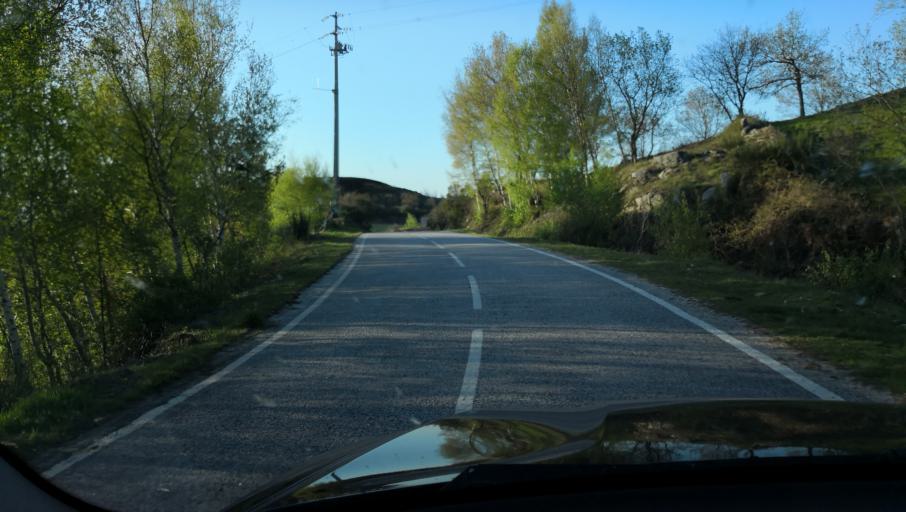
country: PT
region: Vila Real
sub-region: Vila Real
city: Vila Real
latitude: 41.3937
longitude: -7.8266
